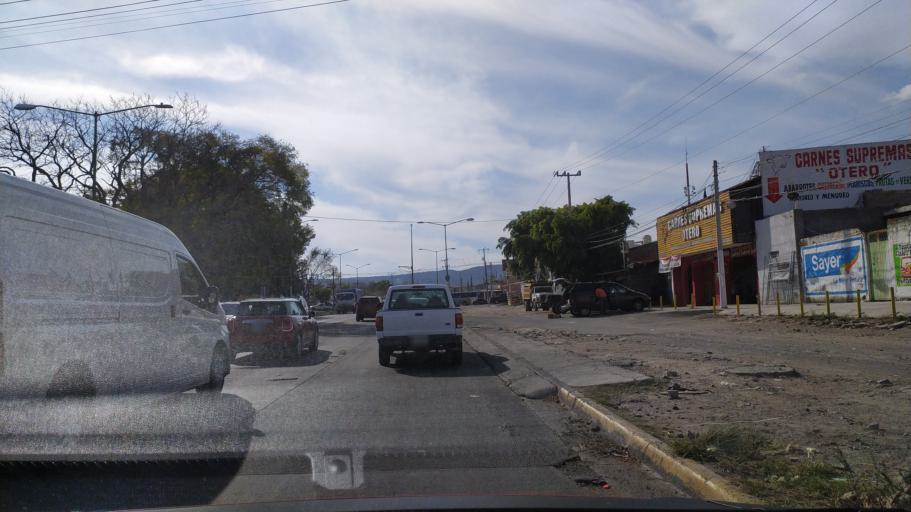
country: MX
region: Jalisco
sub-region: Tlajomulco de Zuniga
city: Palomar
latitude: 20.6289
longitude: -103.4538
